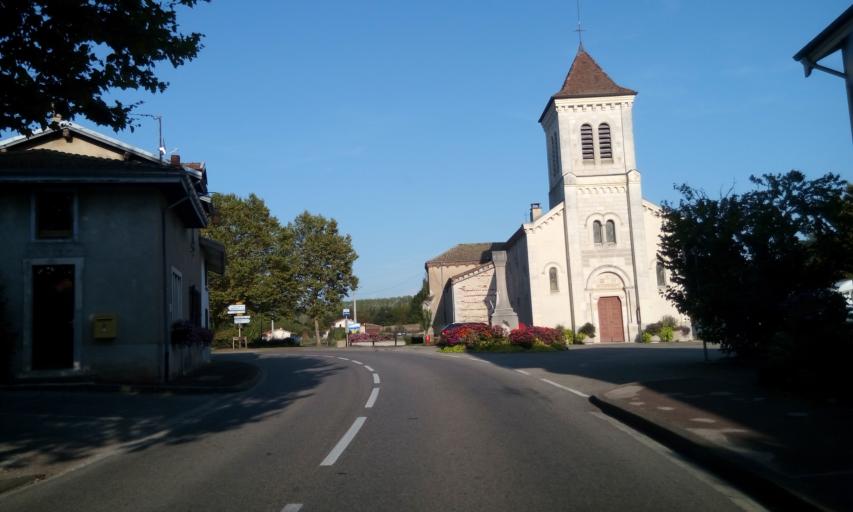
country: FR
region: Rhone-Alpes
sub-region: Departement de l'Ain
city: Chalamont
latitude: 45.9800
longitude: 5.1044
